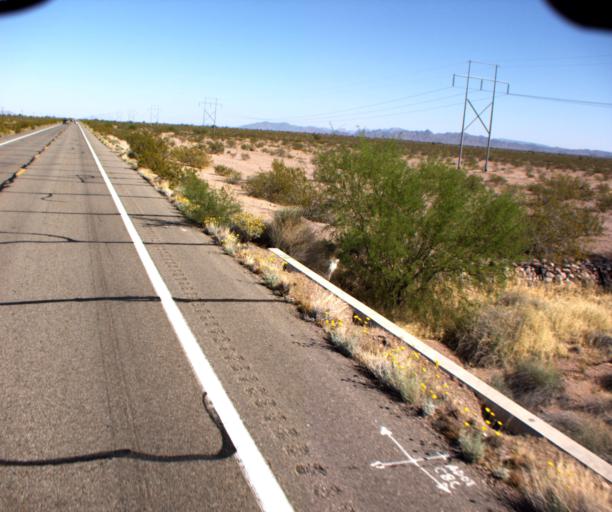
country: US
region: Arizona
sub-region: La Paz County
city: Quartzsite
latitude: 33.3640
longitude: -114.2171
